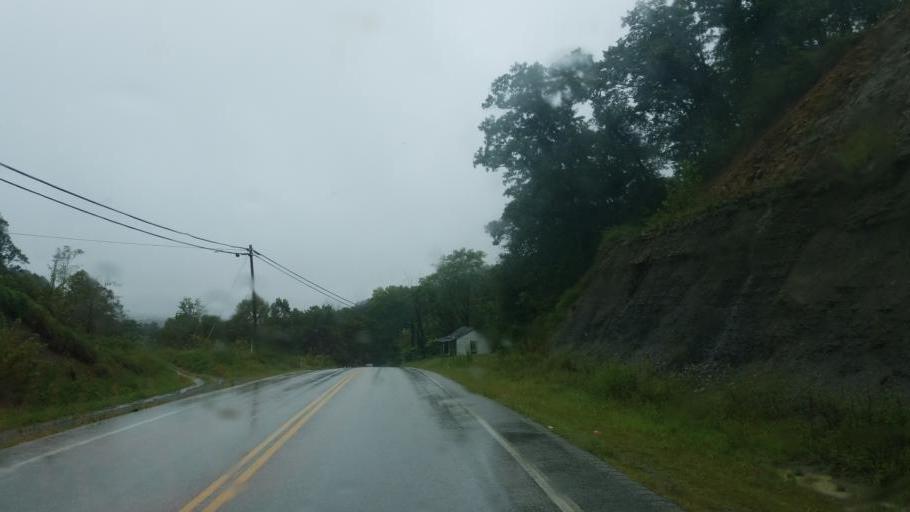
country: US
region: Kentucky
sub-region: Greenup County
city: South Shore
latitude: 38.7140
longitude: -82.9554
